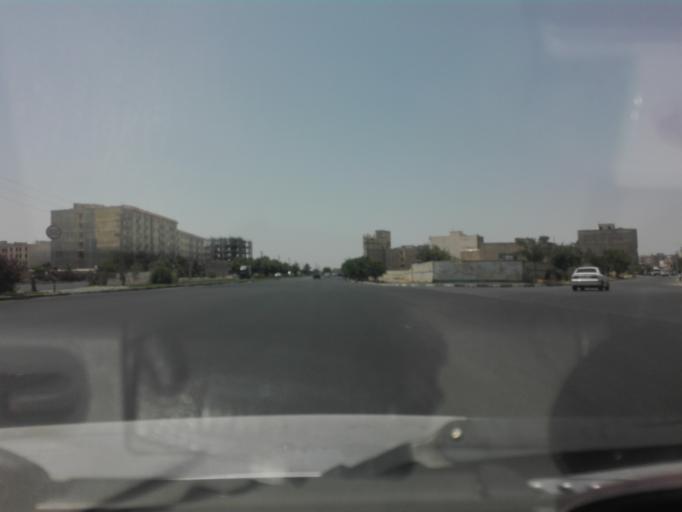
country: IR
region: Tehran
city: Malard
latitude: 35.7118
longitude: 50.9771
